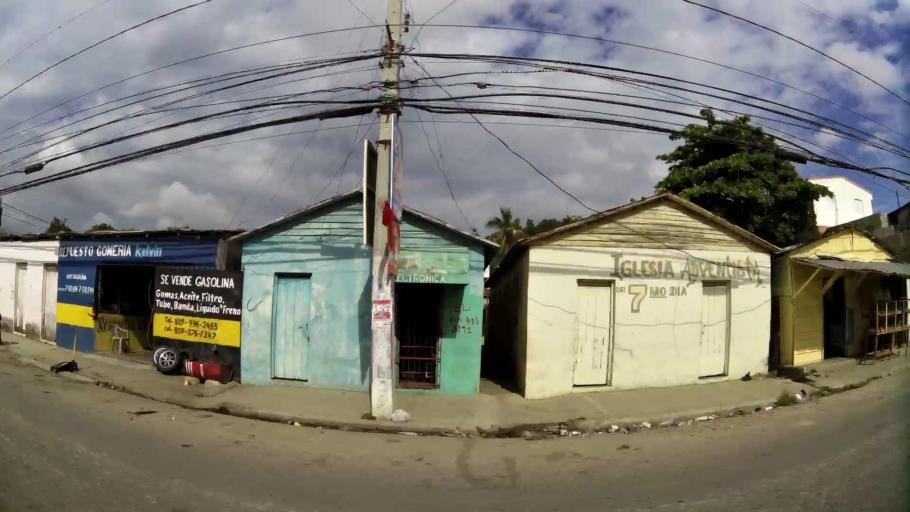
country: DO
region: Santiago
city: Santiago de los Caballeros
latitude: 19.4240
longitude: -70.7134
